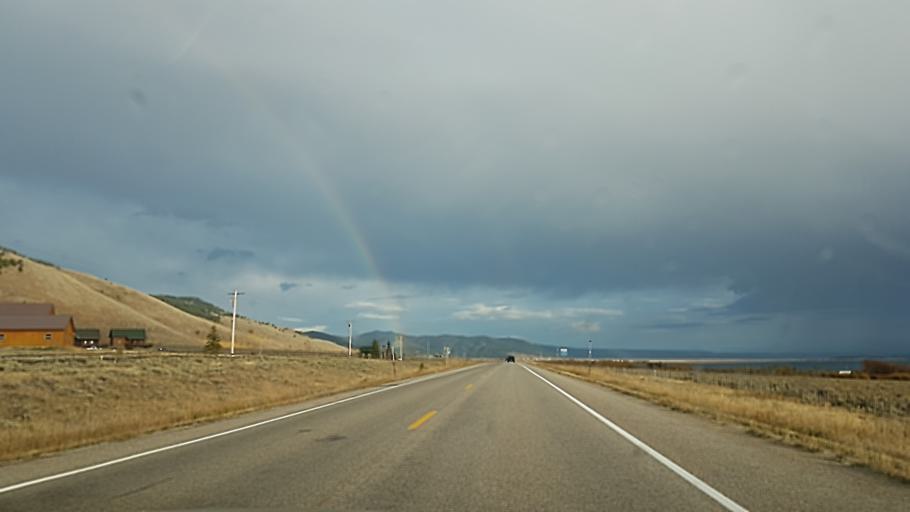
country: US
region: Montana
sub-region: Gallatin County
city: West Yellowstone
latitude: 44.6800
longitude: -111.4259
